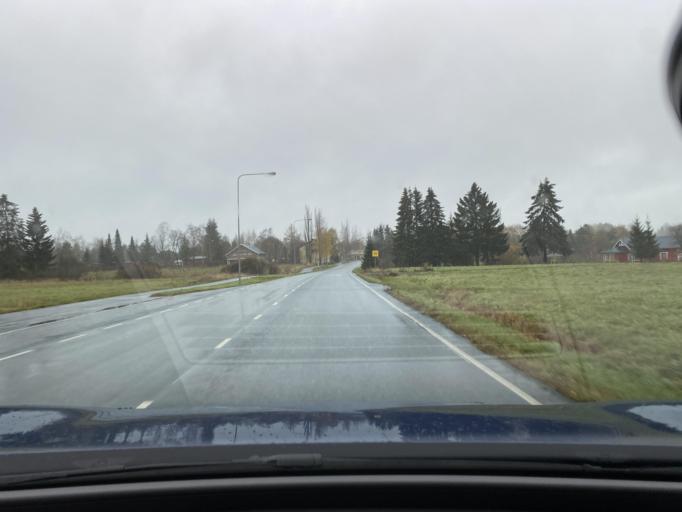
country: FI
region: Varsinais-Suomi
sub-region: Loimaa
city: Alastaro
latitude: 60.9447
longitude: 22.8657
